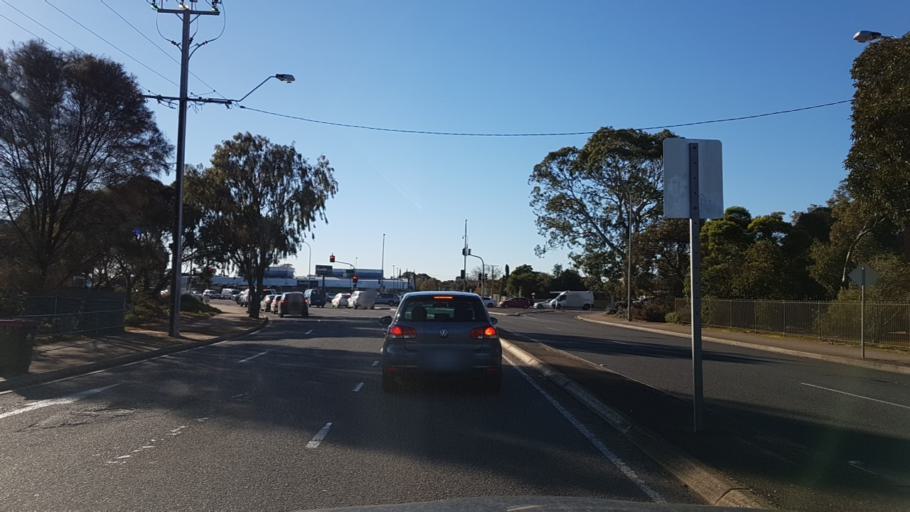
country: AU
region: South Australia
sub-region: Marion
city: Sturt
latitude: -35.0185
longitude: 138.5497
